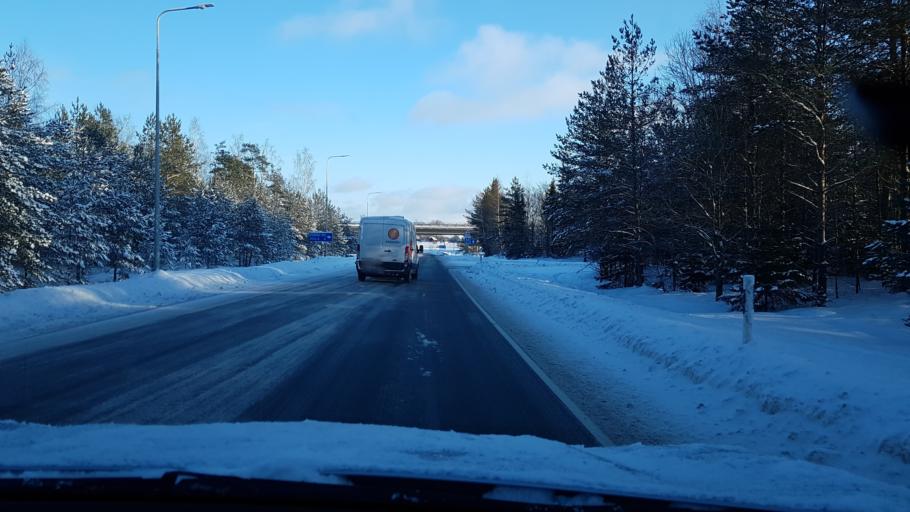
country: EE
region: Harju
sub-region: Keila linn
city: Keila
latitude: 59.2413
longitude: 24.4895
